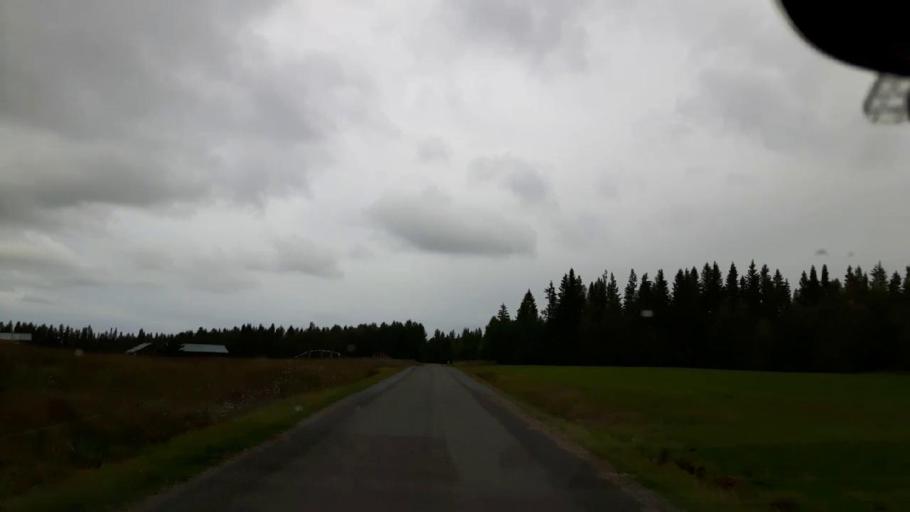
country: SE
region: Jaemtland
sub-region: OEstersunds Kommun
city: Ostersund
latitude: 63.0763
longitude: 14.5543
